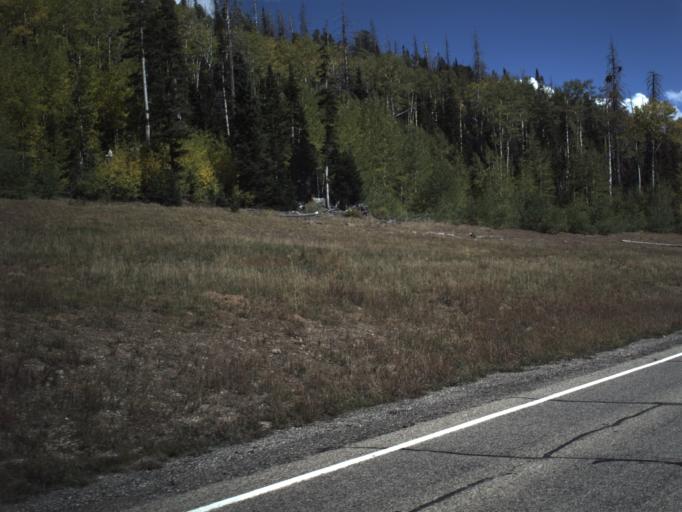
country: US
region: Utah
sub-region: Iron County
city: Cedar City
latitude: 37.5722
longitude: -112.8201
